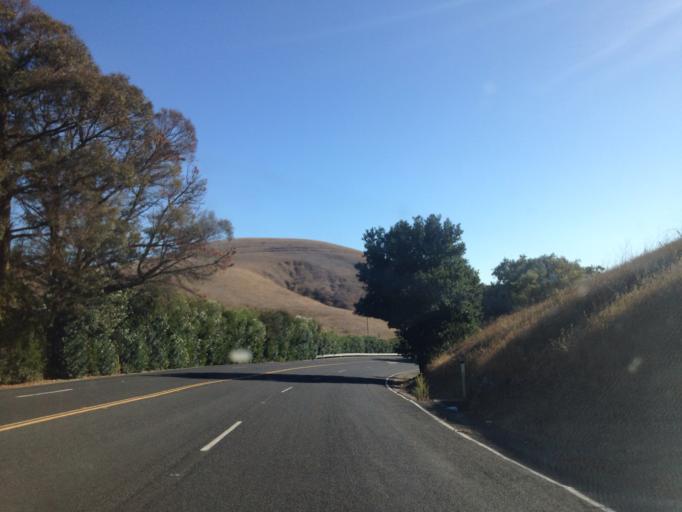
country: US
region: California
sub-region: Contra Costa County
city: Crockett
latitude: 38.0538
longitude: -122.2415
